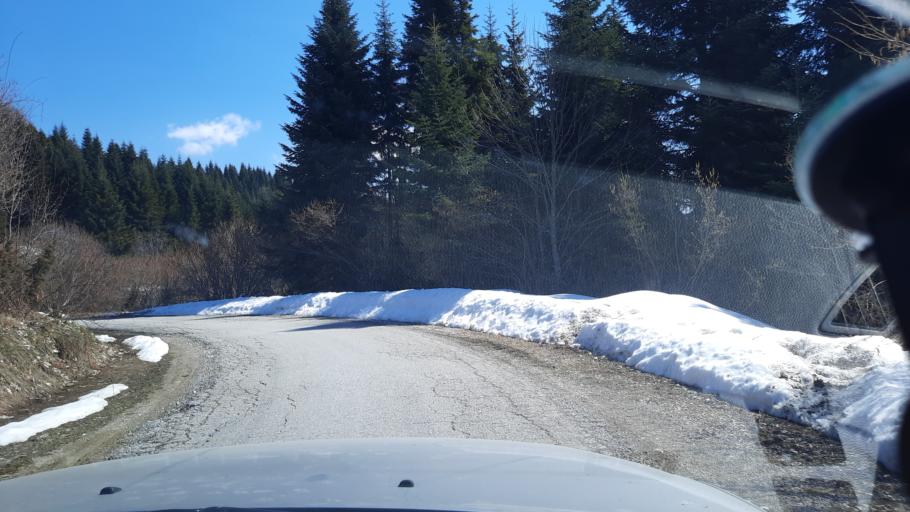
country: MK
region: Gostivar
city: Vrutok
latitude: 41.7068
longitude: 20.7376
